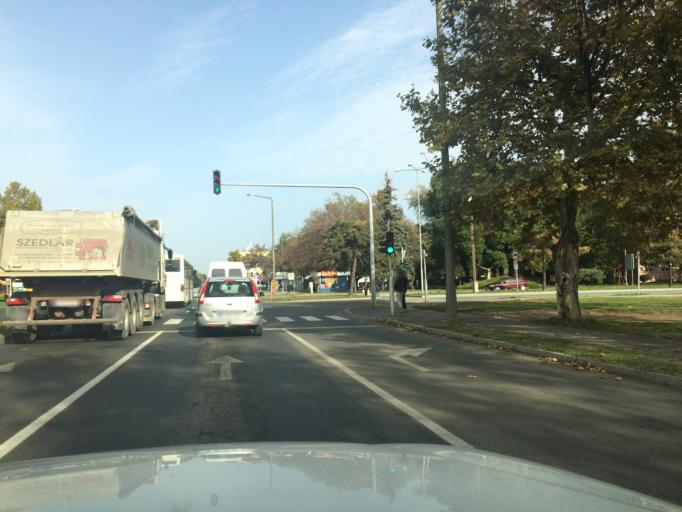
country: HU
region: Szabolcs-Szatmar-Bereg
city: Nyiregyhaza
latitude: 47.9463
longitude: 21.7069
